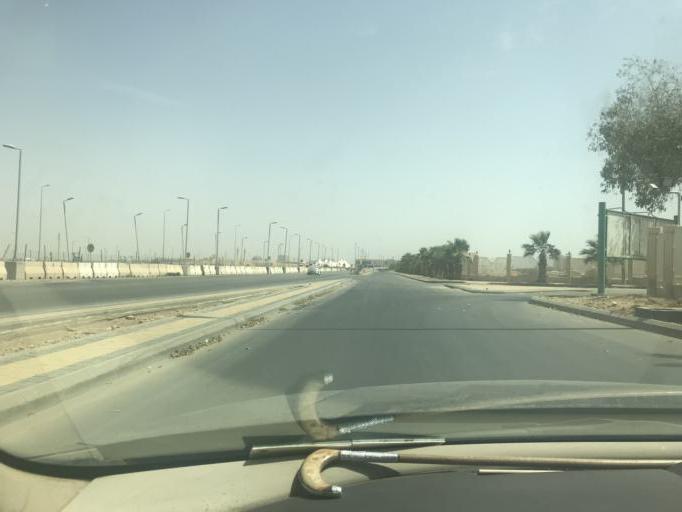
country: SA
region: Ar Riyad
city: Riyadh
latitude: 24.8287
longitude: 46.6951
